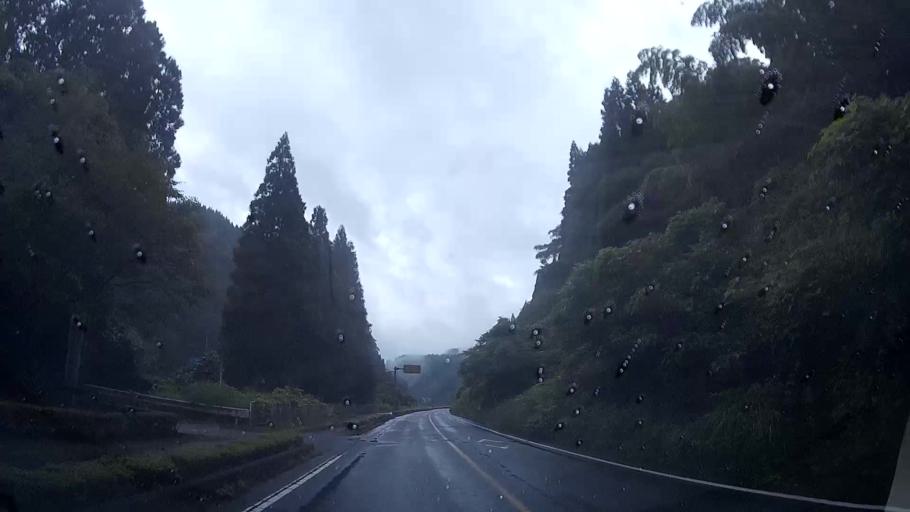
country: JP
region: Oita
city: Tsukawaki
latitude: 33.1790
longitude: 131.0360
